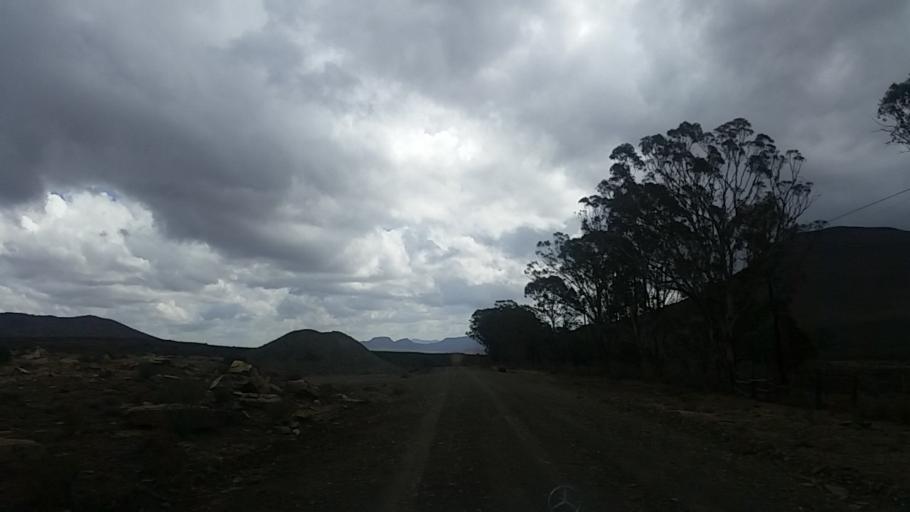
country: ZA
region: Eastern Cape
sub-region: Chris Hani District Municipality
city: Middelburg
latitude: -31.7894
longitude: 24.6742
